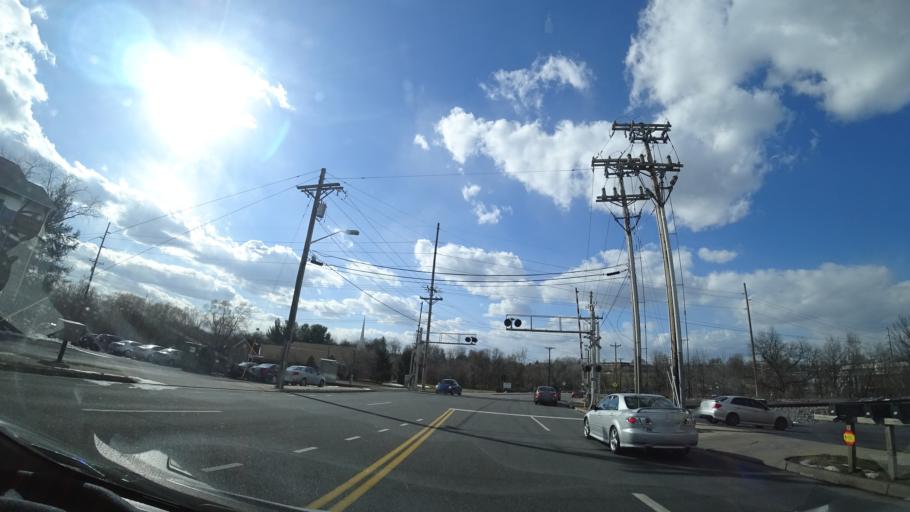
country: US
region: Virginia
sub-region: City of Harrisonburg
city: Harrisonburg
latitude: 38.4363
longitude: -78.8805
